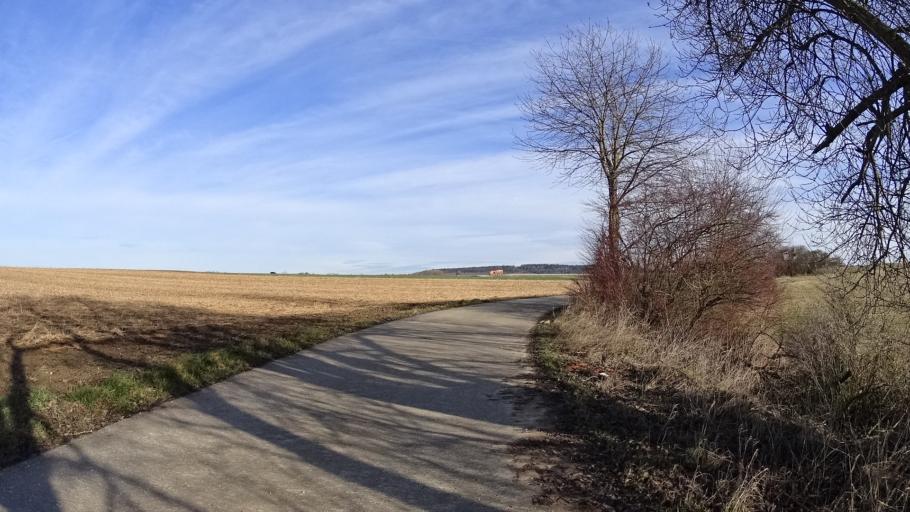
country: DE
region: Bavaria
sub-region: Upper Bavaria
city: Eitensheim
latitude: 48.8224
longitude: 11.3408
